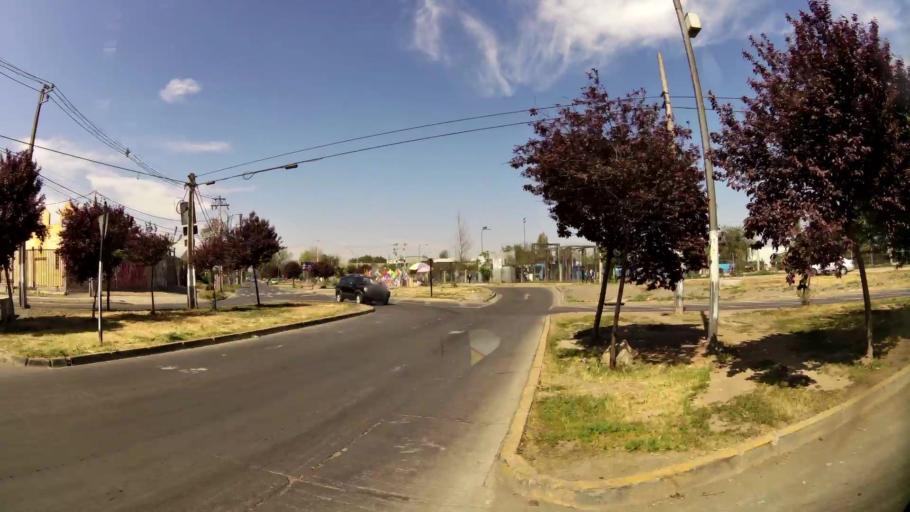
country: CL
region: Santiago Metropolitan
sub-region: Provincia de Santiago
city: Lo Prado
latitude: -33.4019
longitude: -70.7312
